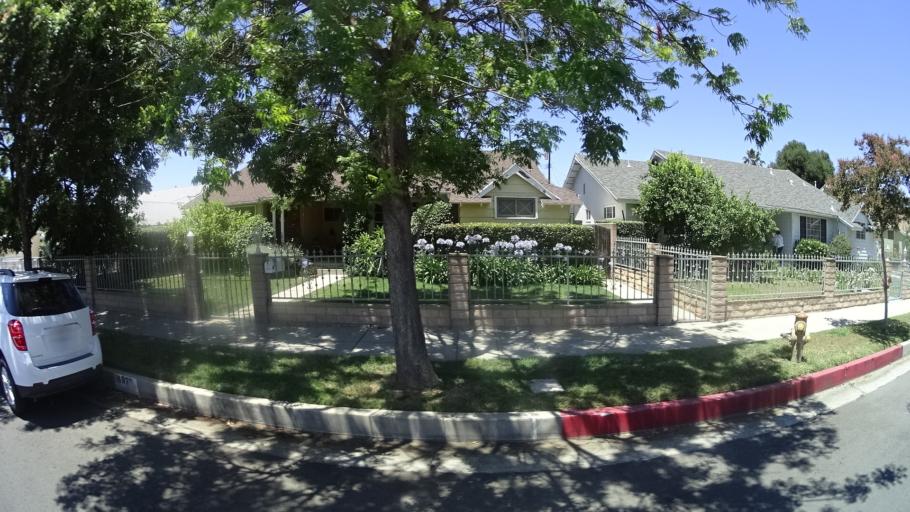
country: US
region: California
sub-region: Los Angeles County
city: Northridge
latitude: 34.1967
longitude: -118.5100
